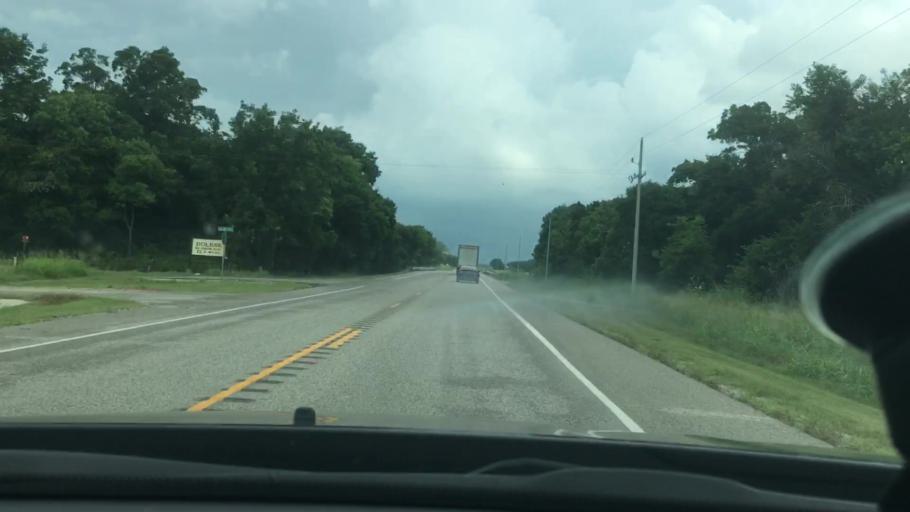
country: US
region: Oklahoma
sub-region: Murray County
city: Sulphur
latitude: 34.3610
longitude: -96.9508
